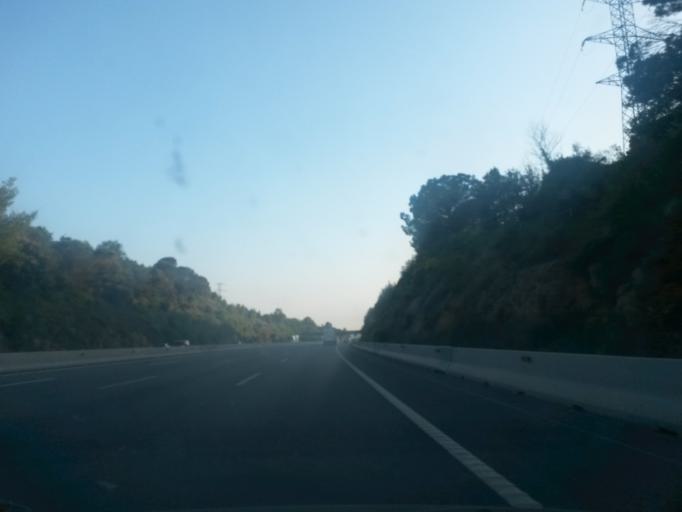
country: ES
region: Catalonia
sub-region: Provincia de Girona
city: Girona
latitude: 42.0044
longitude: 2.8063
